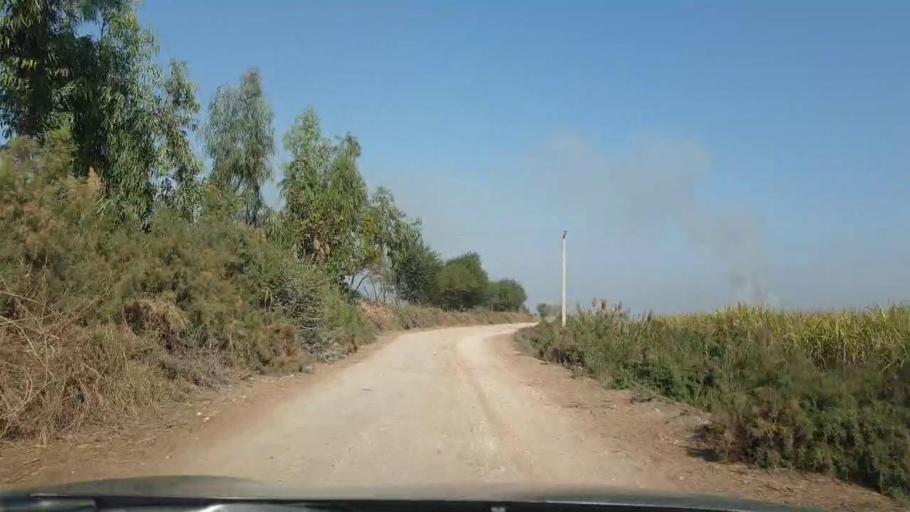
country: PK
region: Sindh
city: Berani
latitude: 25.6445
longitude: 68.8960
